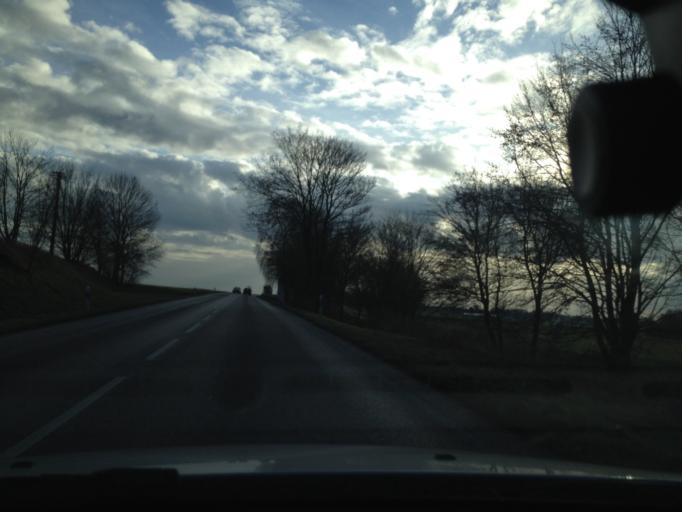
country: DE
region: Bavaria
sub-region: Swabia
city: Grossaitingen
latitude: 48.2198
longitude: 10.7766
